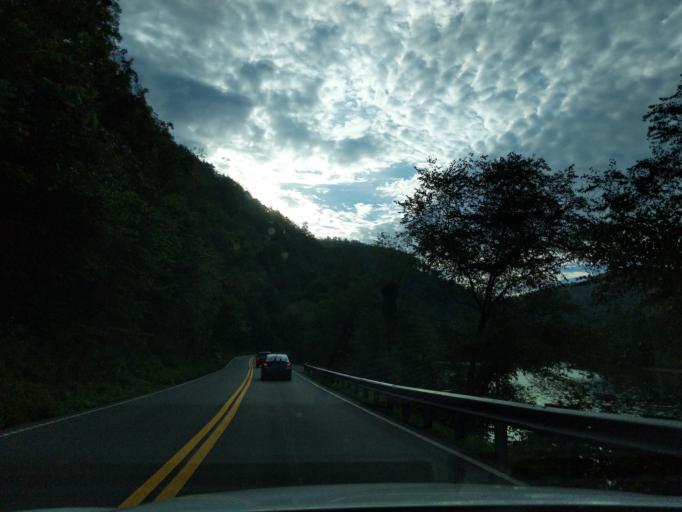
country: US
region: Tennessee
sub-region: Polk County
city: Benton
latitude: 35.0994
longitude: -84.5545
